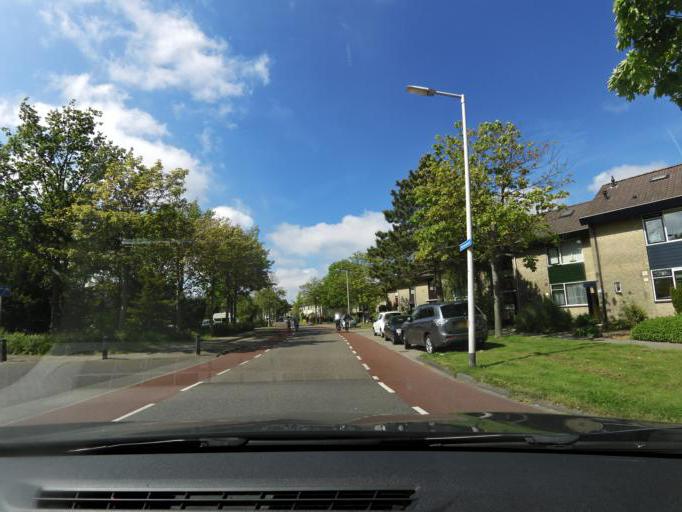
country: NL
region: South Holland
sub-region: Gemeente Hellevoetsluis
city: Nieuw-Helvoet
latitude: 51.8685
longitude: 4.0718
